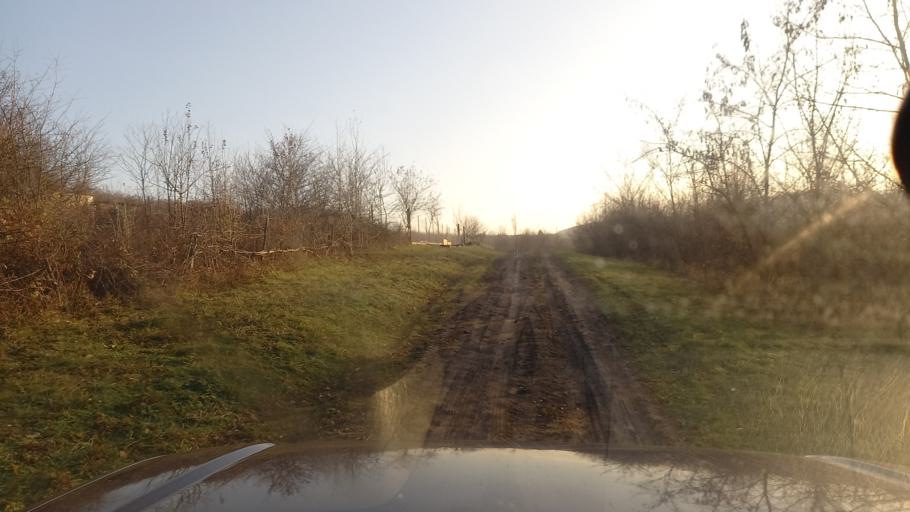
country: RU
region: Krasnodarskiy
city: Il'skiy
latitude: 44.8182
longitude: 38.5950
